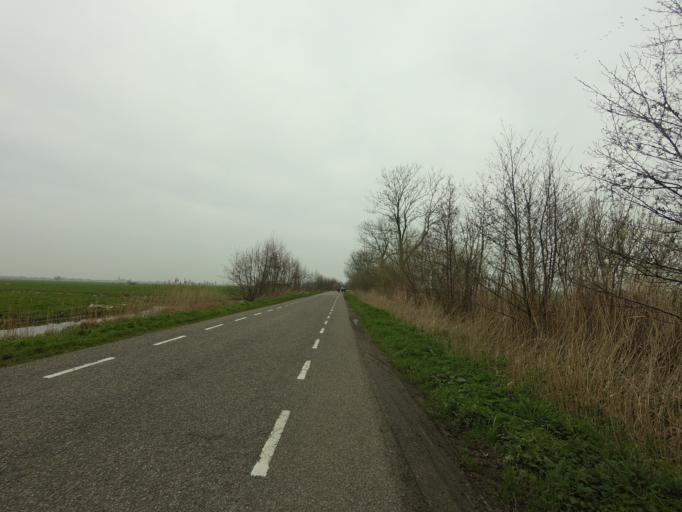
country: NL
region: Utrecht
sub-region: Stichtse Vecht
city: Breukelen
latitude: 52.1930
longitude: 4.9594
